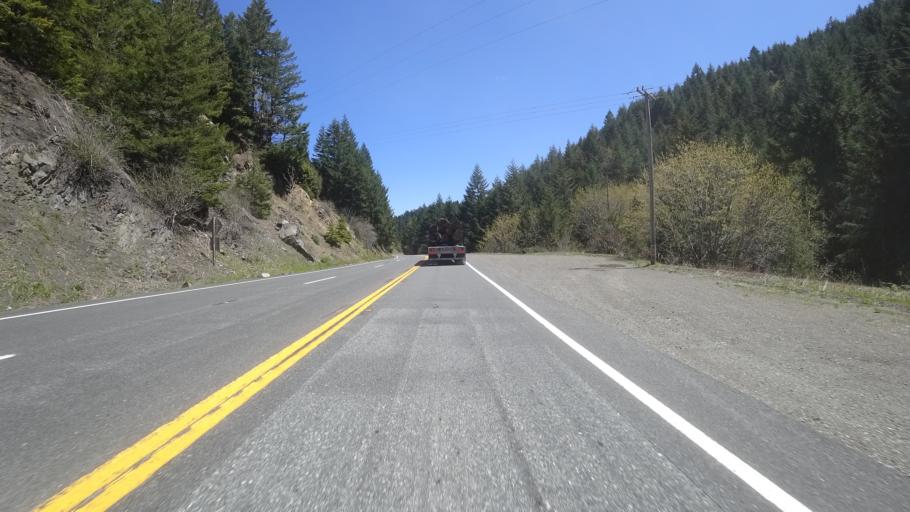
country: US
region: California
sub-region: Humboldt County
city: Willow Creek
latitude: 40.9028
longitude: -123.7660
